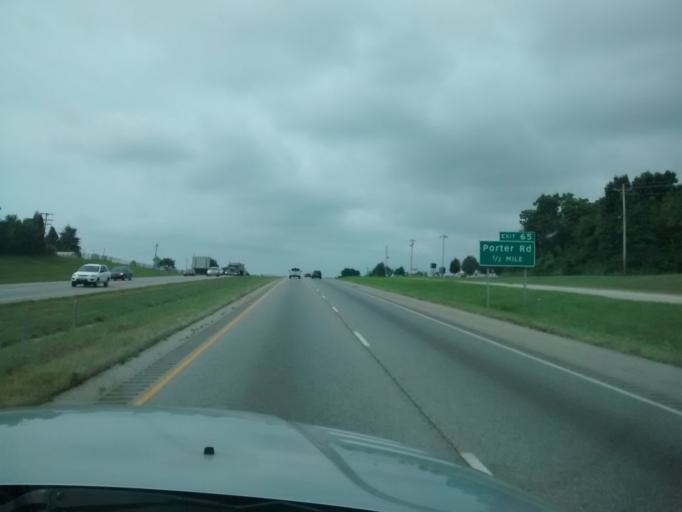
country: US
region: Arkansas
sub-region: Washington County
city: Johnson
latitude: 36.0997
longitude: -94.1852
